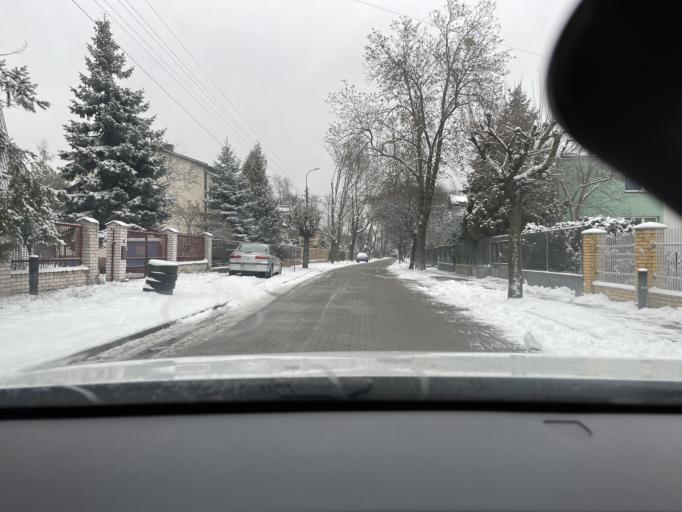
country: PL
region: Masovian Voivodeship
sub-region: Powiat zyrardowski
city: Zyrardow
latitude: 52.0557
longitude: 20.4558
